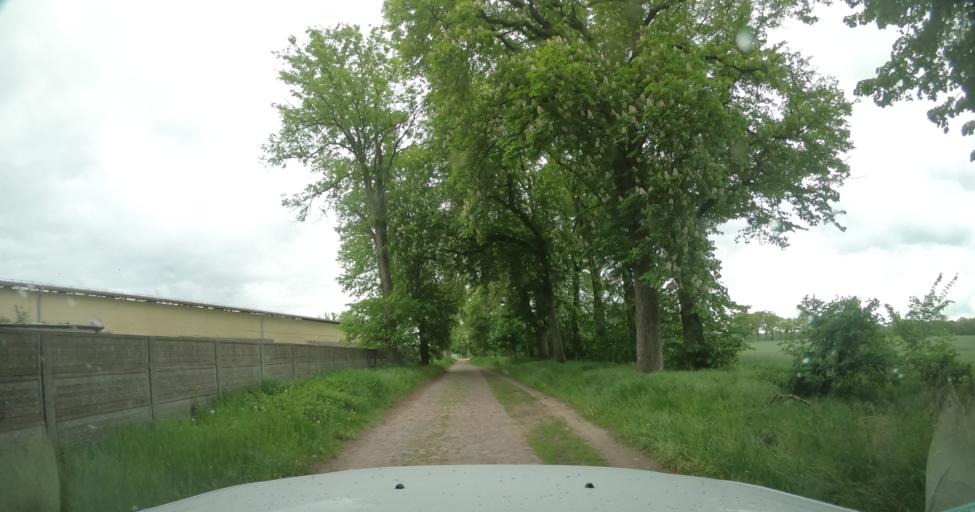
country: PL
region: West Pomeranian Voivodeship
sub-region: Powiat stargardzki
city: Suchan
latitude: 53.2516
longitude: 15.2583
